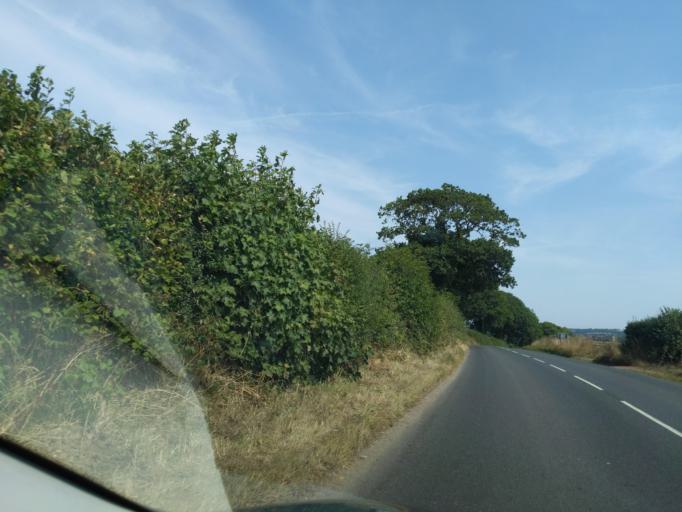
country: GB
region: England
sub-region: Devon
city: Winkleigh
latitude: 50.7927
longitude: -3.9504
